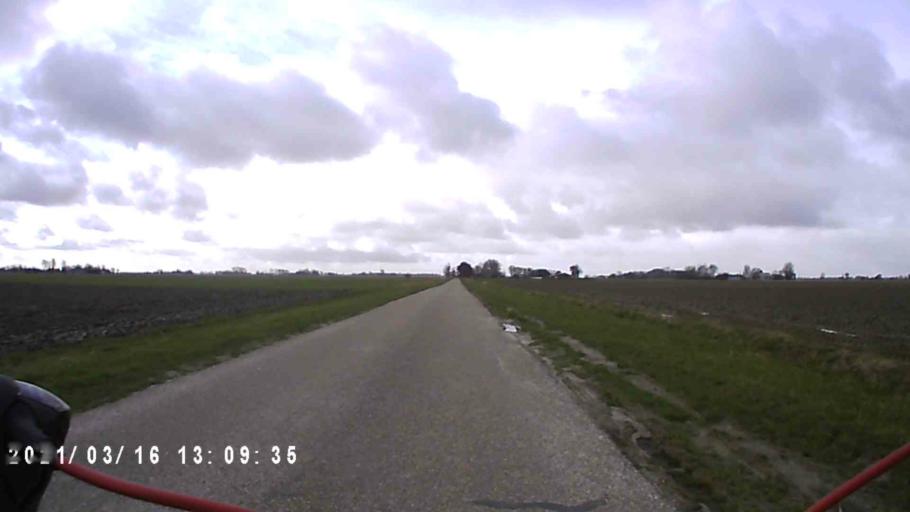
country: NL
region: Friesland
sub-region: Menameradiel
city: Berltsum
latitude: 53.2454
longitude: 5.6254
